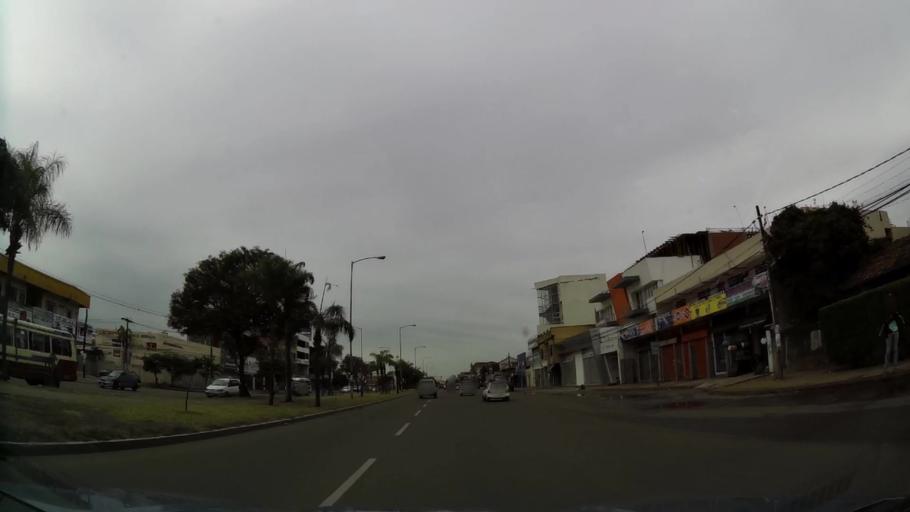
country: BO
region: Santa Cruz
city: Santa Cruz de la Sierra
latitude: -17.8030
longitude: -63.1982
